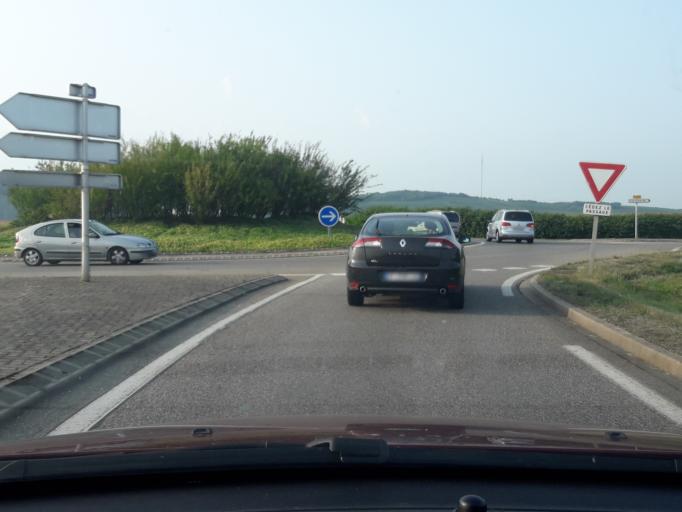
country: FR
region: Alsace
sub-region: Departement du Bas-Rhin
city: Irmstett
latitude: 48.6051
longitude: 7.4801
